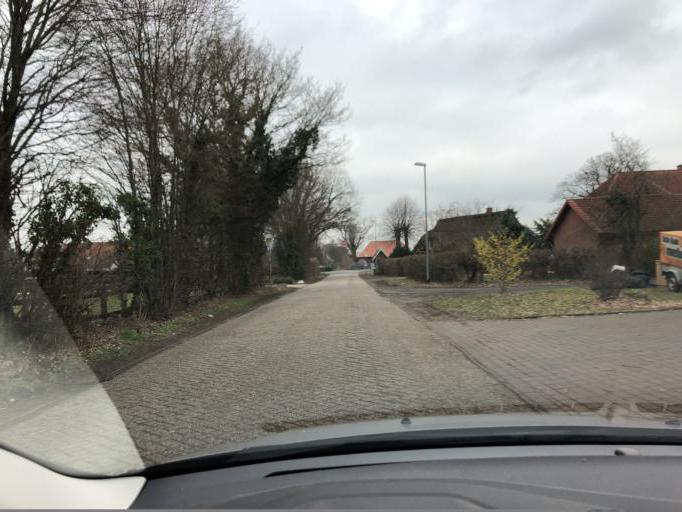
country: DE
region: Lower Saxony
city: Ganderkesee
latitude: 53.0953
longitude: 8.5691
